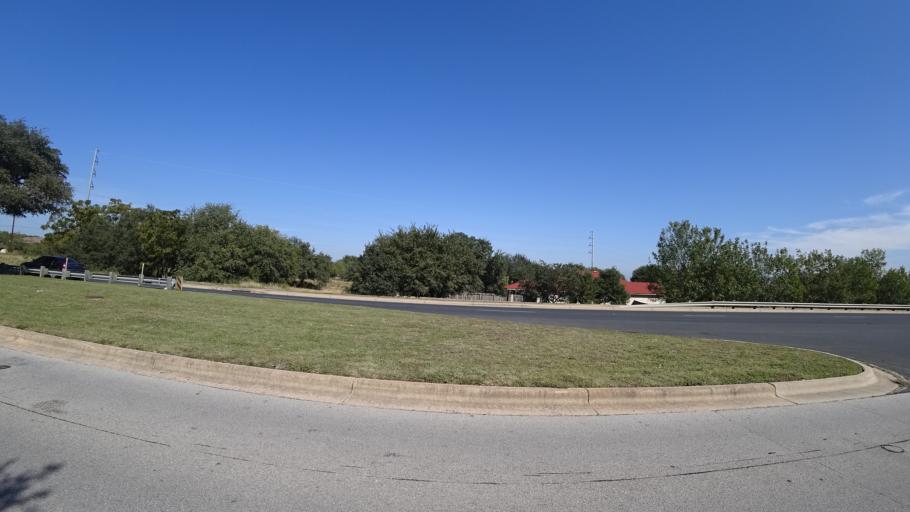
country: US
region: Texas
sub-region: Travis County
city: Shady Hollow
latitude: 30.1965
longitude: -97.8605
